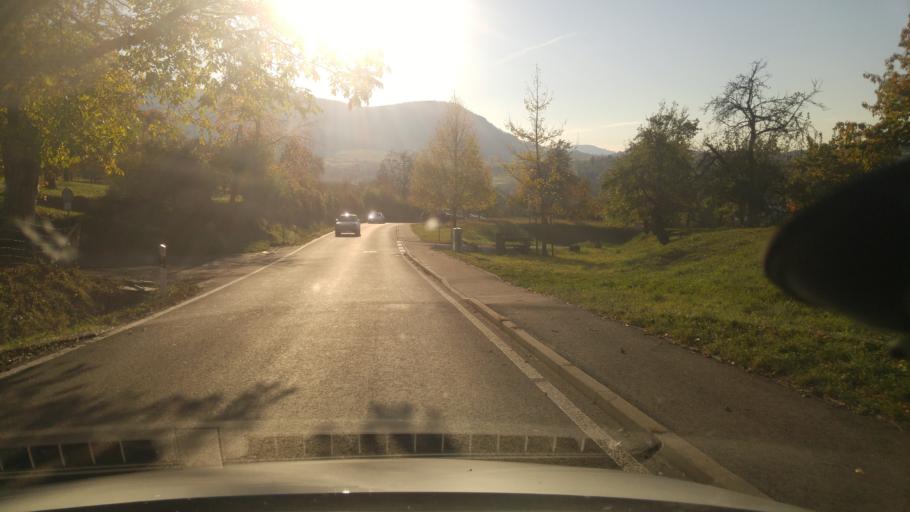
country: DE
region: Baden-Wuerttemberg
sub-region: Regierungsbezirk Stuttgart
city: Owen
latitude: 48.5893
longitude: 9.4574
